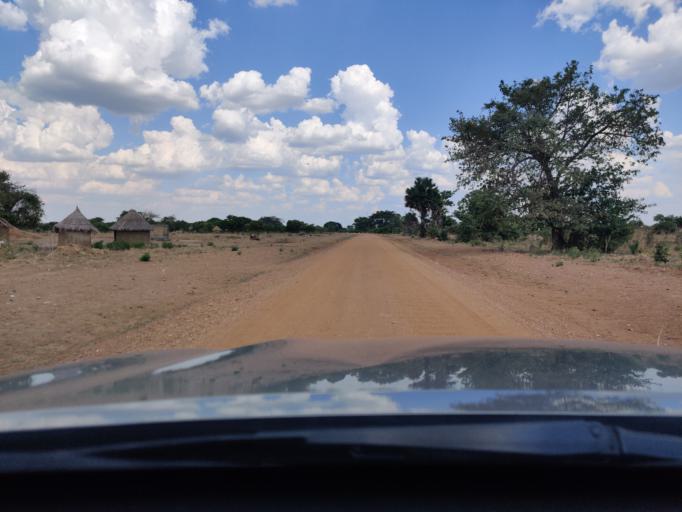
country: ZM
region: Central
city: Chibombo
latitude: -14.7608
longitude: 27.8881
